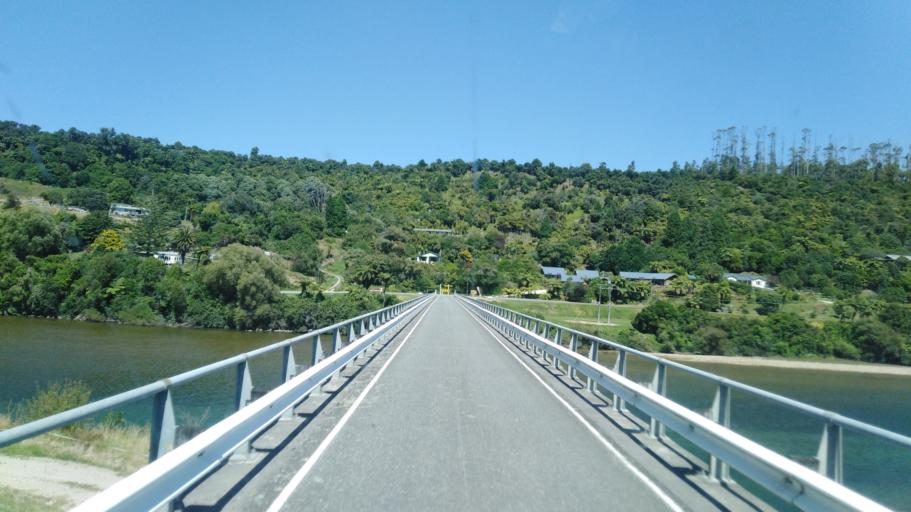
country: NZ
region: West Coast
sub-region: Buller District
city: Westport
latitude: -41.2605
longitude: 172.1318
